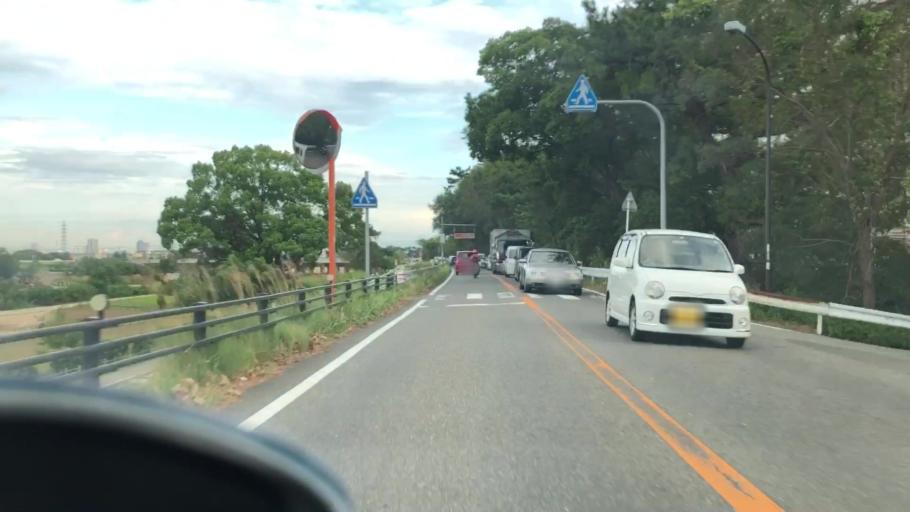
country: JP
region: Hyogo
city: Amagasaki
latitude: 34.7417
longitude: 135.3772
